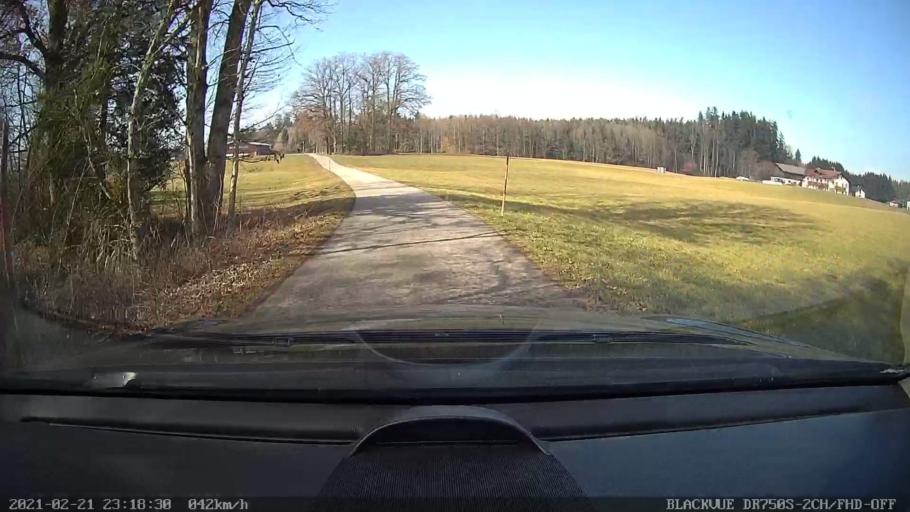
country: DE
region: Bavaria
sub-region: Upper Bavaria
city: Griesstatt
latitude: 48.0043
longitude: 12.2018
